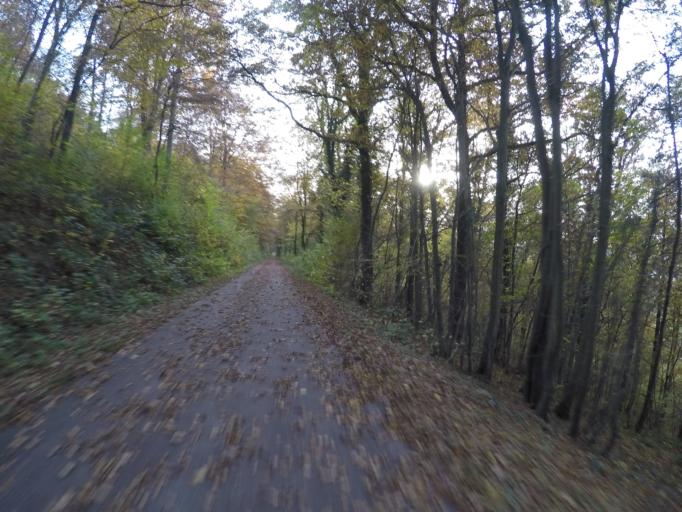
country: BE
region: Wallonia
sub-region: Province du Luxembourg
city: Hotton
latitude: 50.2801
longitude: 5.4815
